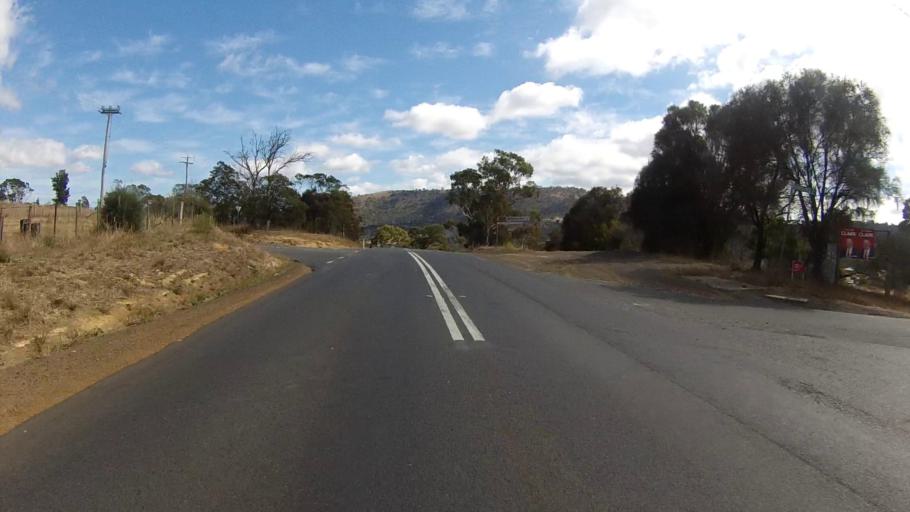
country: AU
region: Tasmania
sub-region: Brighton
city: Old Beach
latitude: -42.7300
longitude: 147.2886
